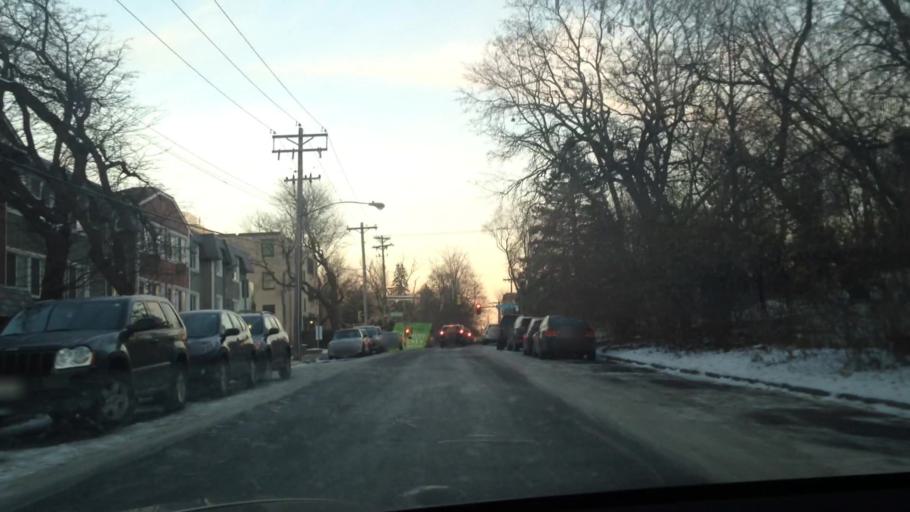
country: US
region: Minnesota
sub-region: Hennepin County
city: Saint Louis Park
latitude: 44.9451
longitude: -93.3248
